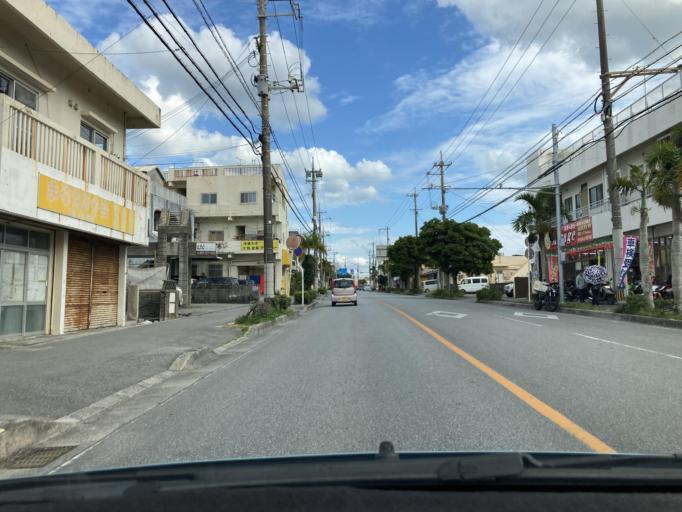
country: JP
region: Okinawa
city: Okinawa
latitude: 26.3610
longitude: 127.8160
